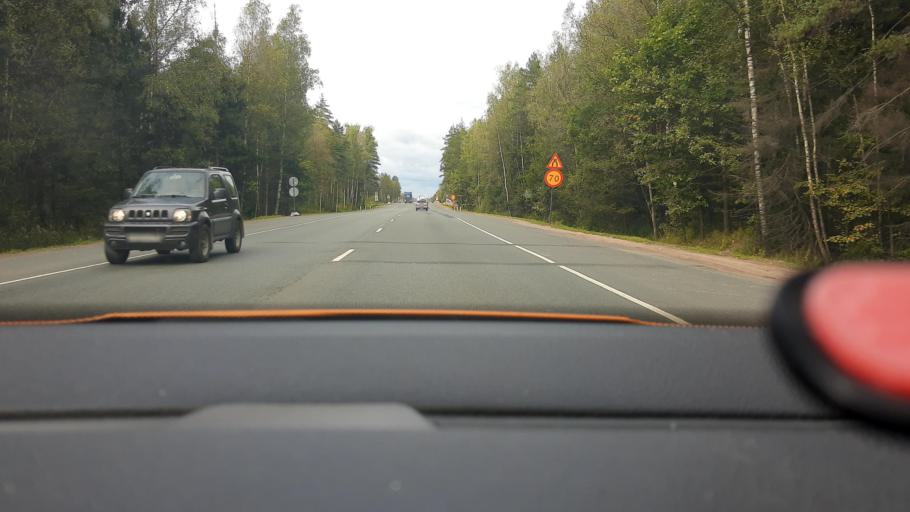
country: RU
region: Moskovskaya
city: Zelenogradskiy
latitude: 56.1005
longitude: 37.9710
